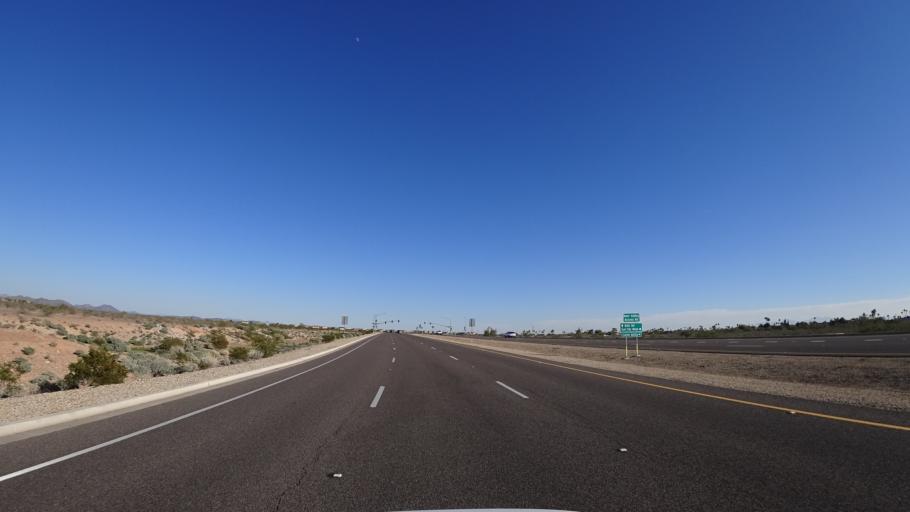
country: US
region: Arizona
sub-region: Maricopa County
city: Sun City West
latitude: 33.6854
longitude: -112.3311
